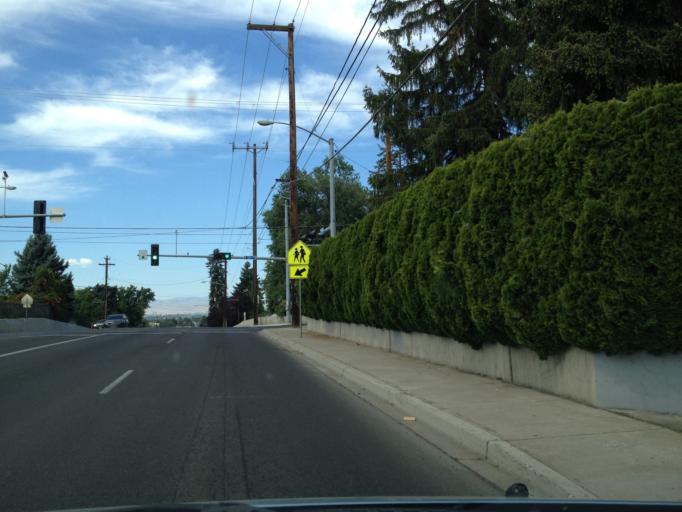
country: US
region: Washington
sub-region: Yakima County
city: Yakima
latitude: 46.5929
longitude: -120.5506
